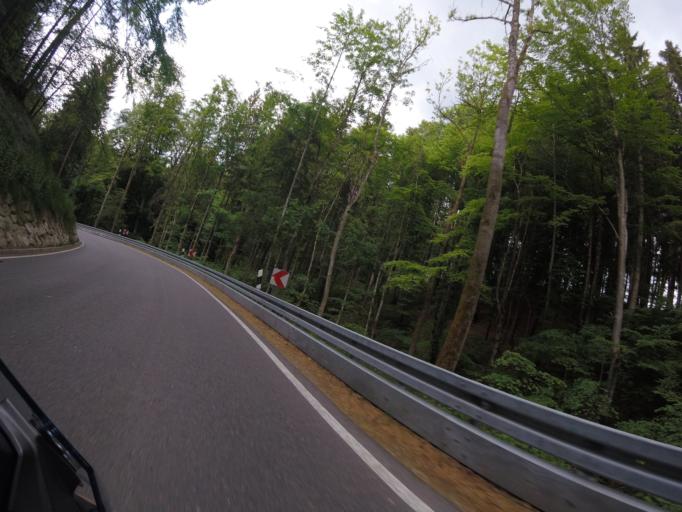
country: DE
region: Bavaria
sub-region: Upper Bavaria
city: Reichertshausen
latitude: 47.8742
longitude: 11.5389
